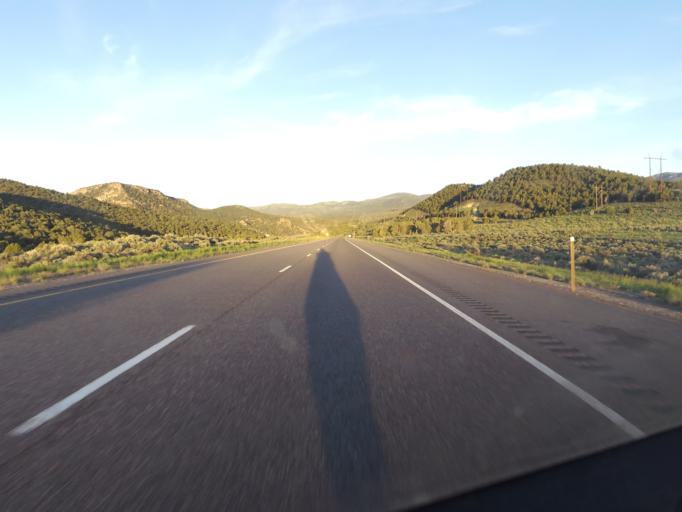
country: US
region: Utah
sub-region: Sevier County
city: Monroe
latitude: 38.5687
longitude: -112.4475
